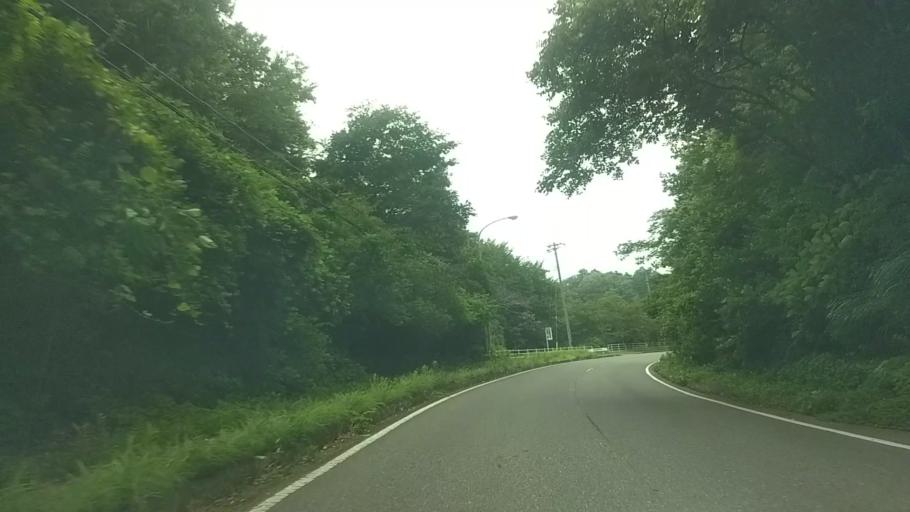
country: JP
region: Chiba
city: Kawaguchi
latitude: 35.2422
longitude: 140.0354
